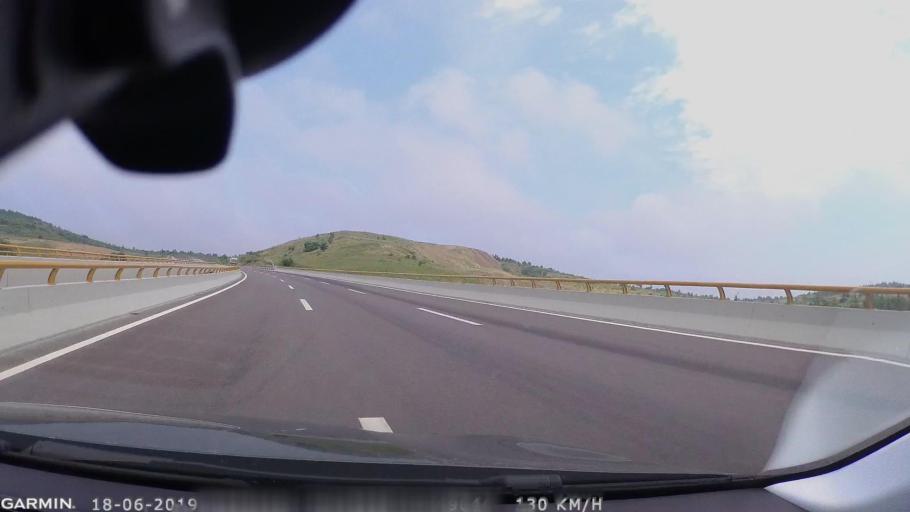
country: MK
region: Petrovec
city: Sredno Konjare
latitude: 41.9441
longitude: 21.7865
